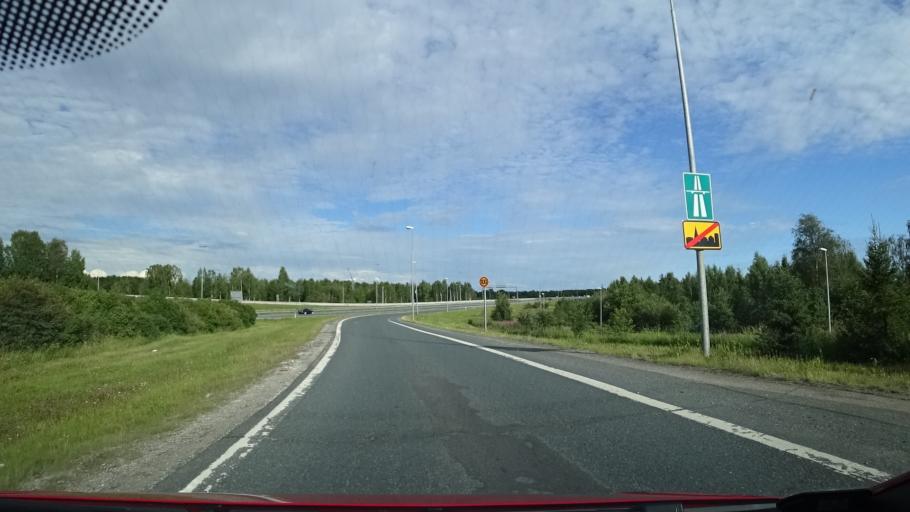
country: FI
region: Lapland
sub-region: Kemi-Tornio
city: Keminmaa
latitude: 65.7918
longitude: 24.5240
